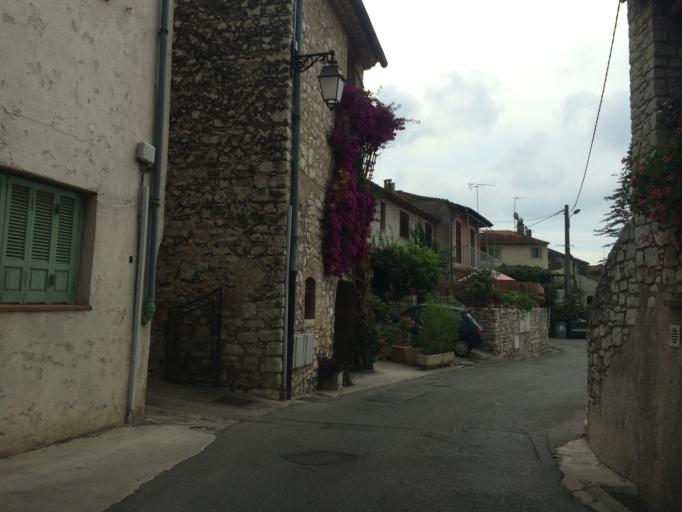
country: FR
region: Provence-Alpes-Cote d'Azur
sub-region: Departement des Alpes-Maritimes
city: La Colle-sur-Loup
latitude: 43.6889
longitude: 7.1015
